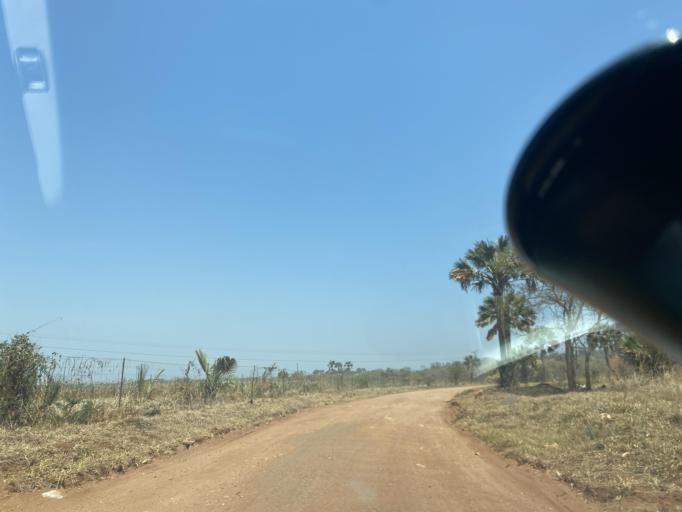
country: ZM
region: Lusaka
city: Kafue
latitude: -15.5492
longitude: 28.0671
